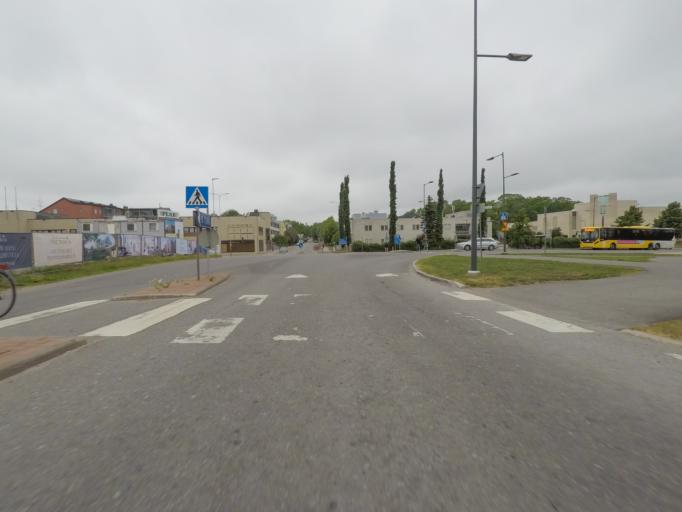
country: FI
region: Varsinais-Suomi
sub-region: Turku
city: Naantali
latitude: 60.4683
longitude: 22.0277
